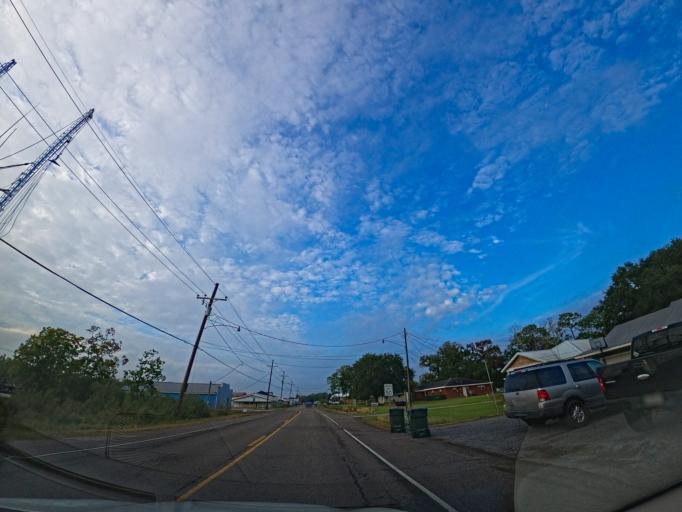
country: US
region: Louisiana
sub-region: Terrebonne Parish
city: Chauvin
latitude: 29.4276
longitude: -90.5999
